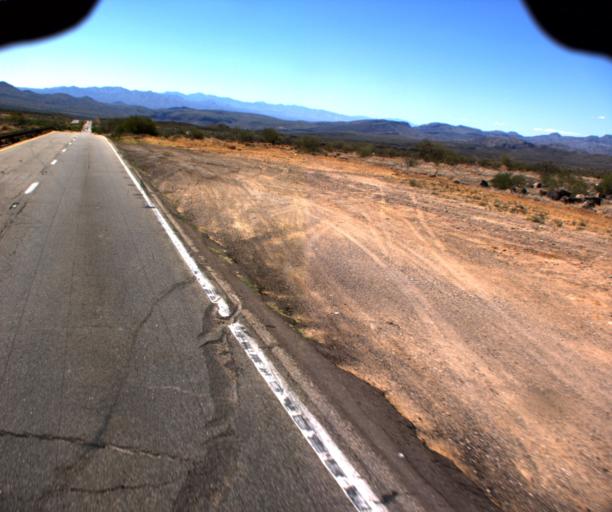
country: US
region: Arizona
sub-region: Yavapai County
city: Bagdad
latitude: 34.4850
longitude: -113.3696
